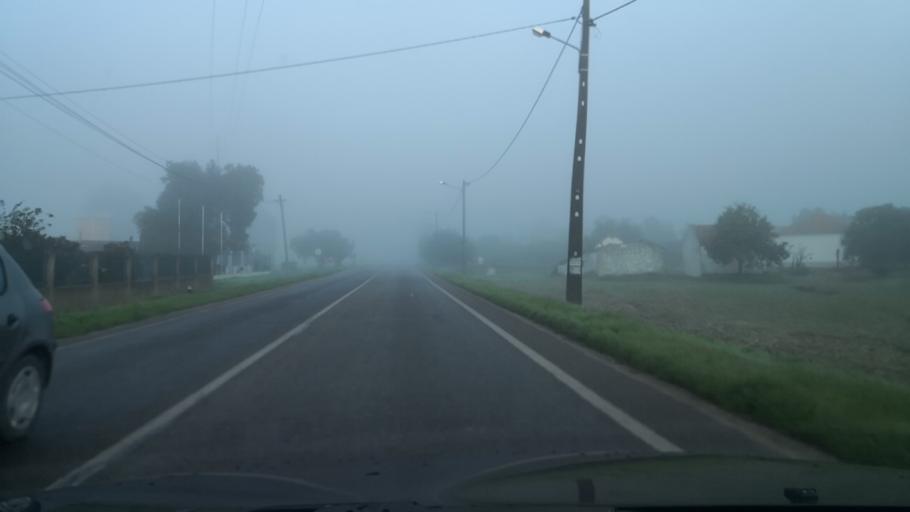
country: PT
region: Setubal
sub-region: Palmela
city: Pinhal Novo
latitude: 38.6142
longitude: -8.9120
